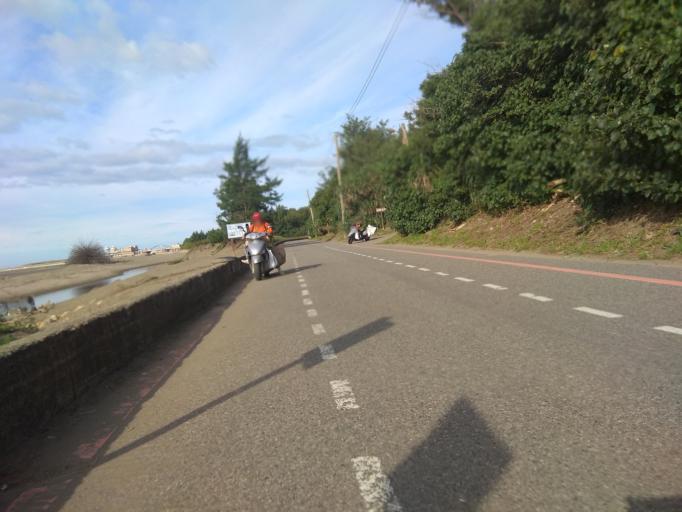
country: TW
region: Taiwan
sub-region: Hsinchu
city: Zhubei
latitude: 24.9789
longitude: 121.0160
